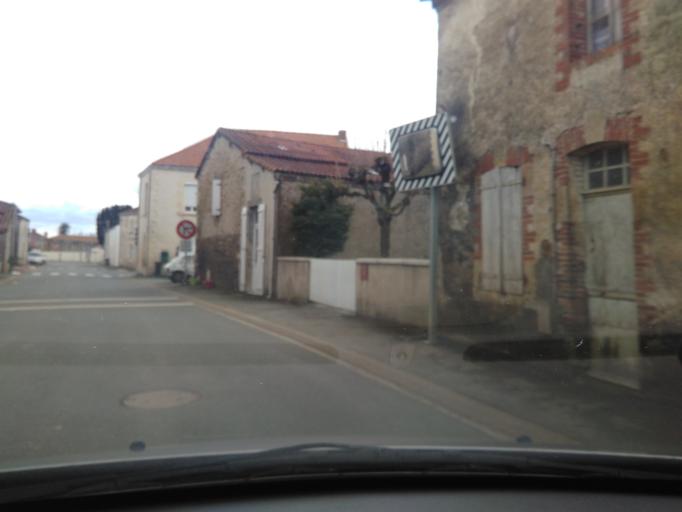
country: FR
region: Pays de la Loire
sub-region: Departement de la Vendee
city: Sainte-Cecile
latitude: 46.6889
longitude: -1.1305
